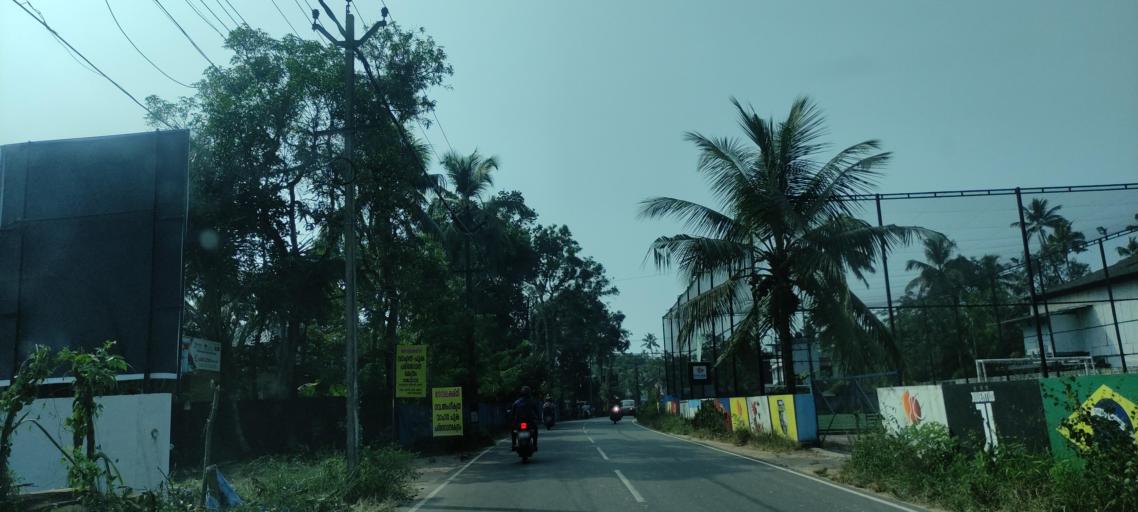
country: IN
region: Kerala
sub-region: Alappuzha
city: Vayalar
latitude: 9.6966
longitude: 76.3215
